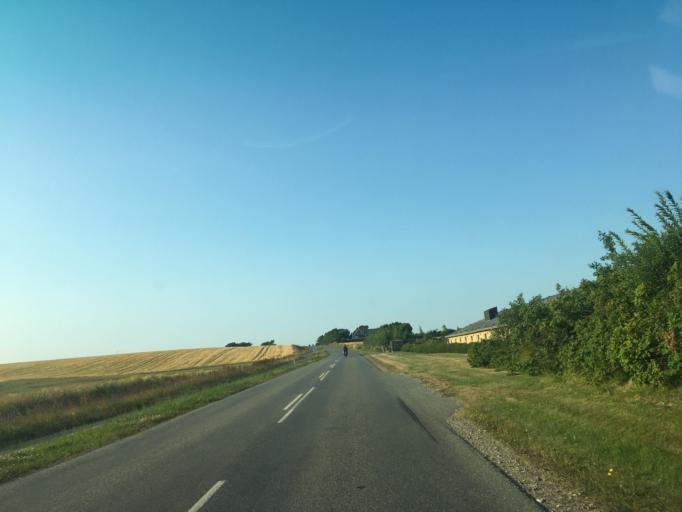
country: DK
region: North Denmark
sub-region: Thisted Kommune
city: Hurup
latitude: 56.7717
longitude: 8.4225
